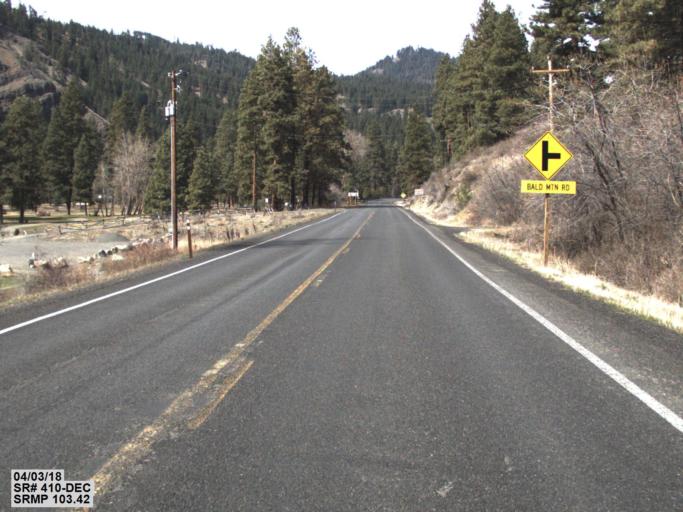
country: US
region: Washington
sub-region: Yakima County
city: Tieton
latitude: 46.8697
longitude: -120.9658
